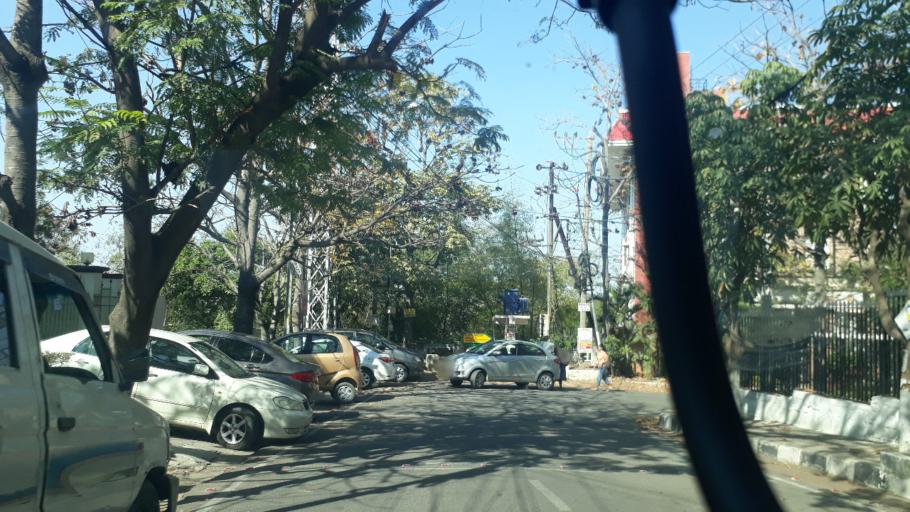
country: IN
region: Telangana
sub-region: Rangareddi
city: Kukatpalli
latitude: 17.4220
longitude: 78.3998
